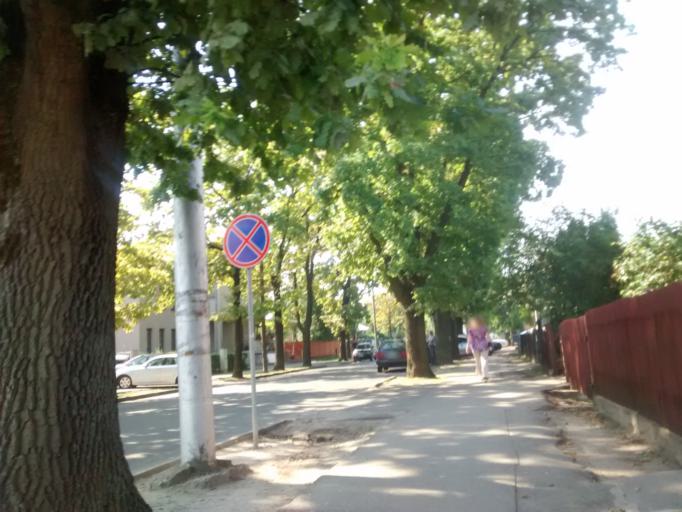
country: LT
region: Kauno apskritis
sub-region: Kaunas
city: Eiguliai
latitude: 54.9170
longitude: 23.9208
